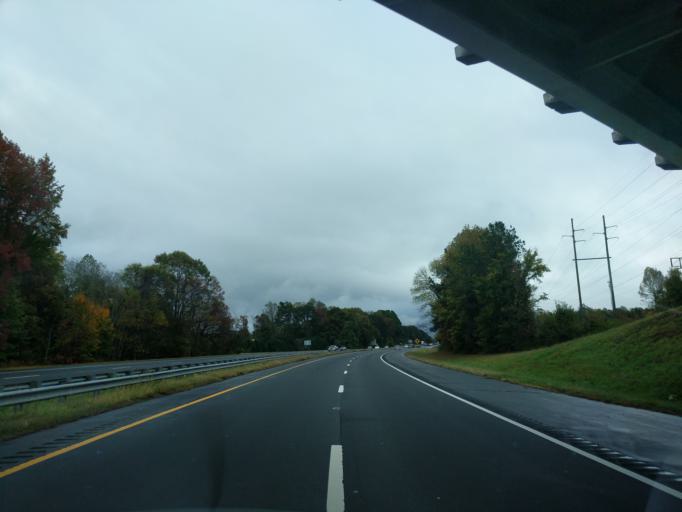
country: US
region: North Carolina
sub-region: Orange County
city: Hillsborough
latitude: 36.0589
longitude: -79.0823
